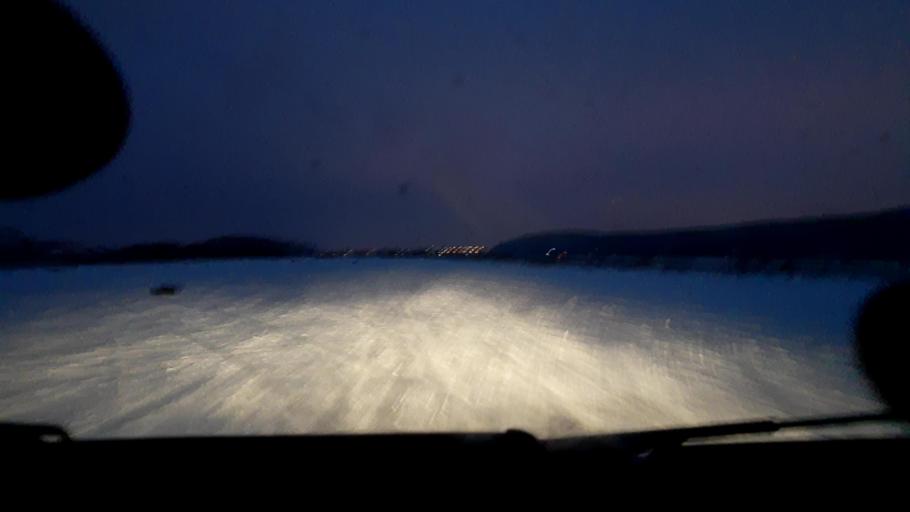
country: RU
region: Bashkortostan
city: Ufa
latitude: 54.8272
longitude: 56.1647
